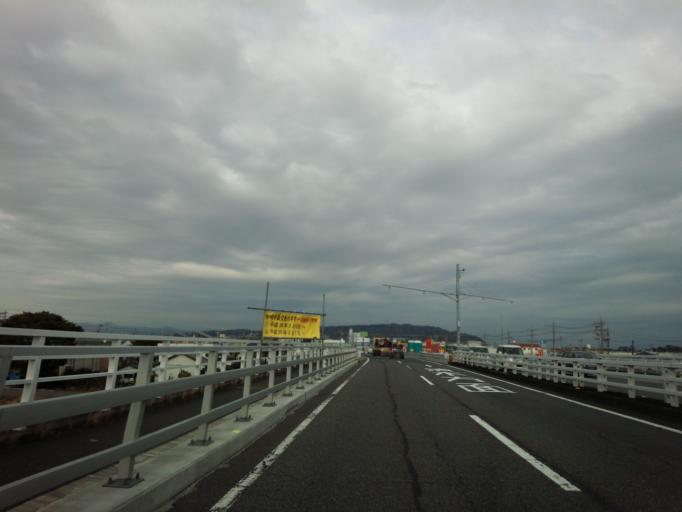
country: JP
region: Shizuoka
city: Shizuoka-shi
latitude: 34.9378
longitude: 138.3914
